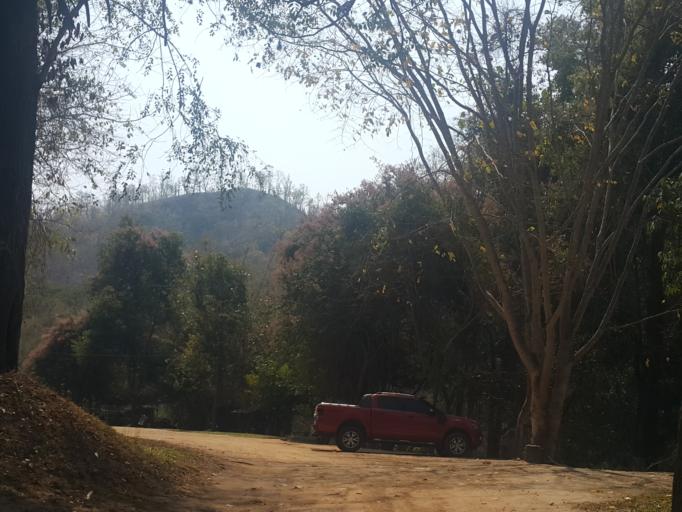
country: TH
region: Chiang Mai
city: Hang Dong
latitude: 18.7200
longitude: 98.8228
